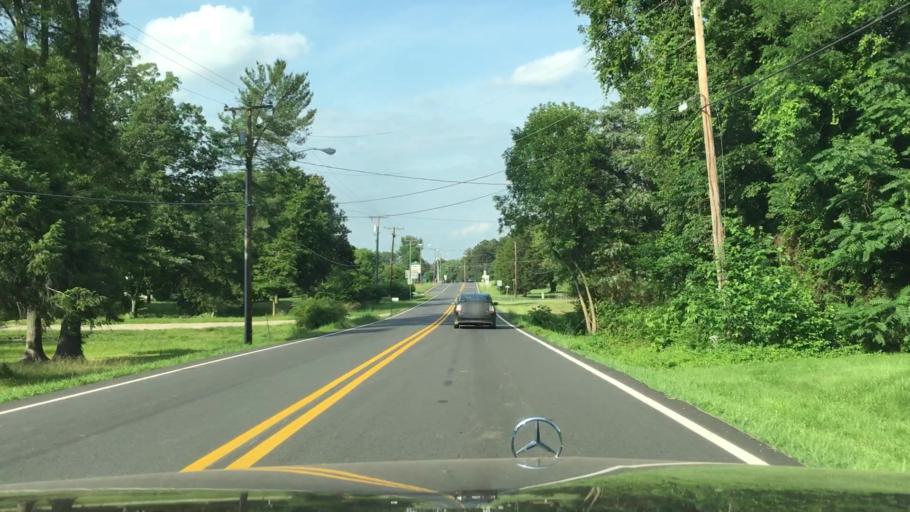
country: US
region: Virginia
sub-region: Orange County
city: Gordonsville
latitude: 38.1380
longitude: -78.1962
